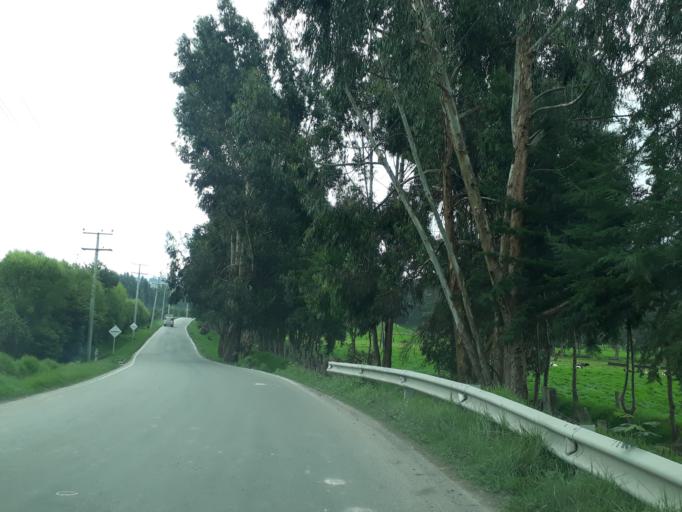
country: CO
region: Cundinamarca
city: Ubate
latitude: 5.3211
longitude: -73.7875
